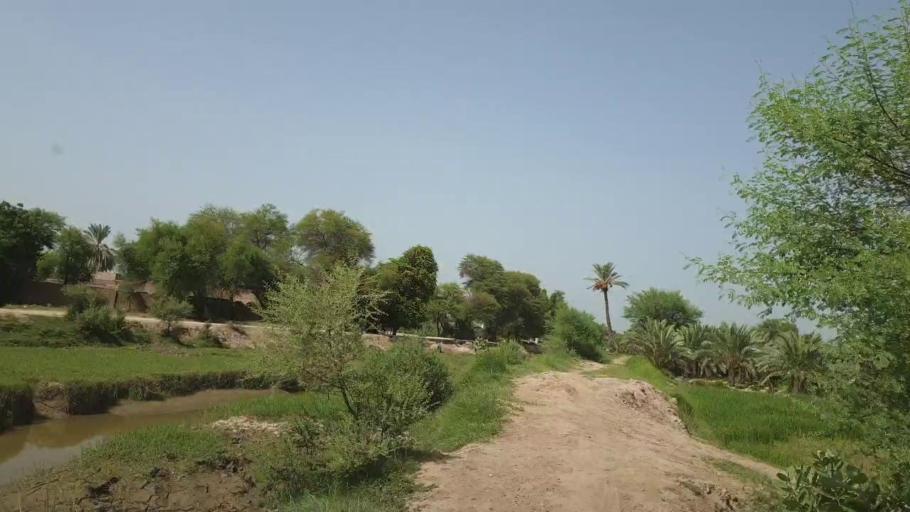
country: PK
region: Sindh
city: Pano Aqil
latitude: 27.8386
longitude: 69.1853
